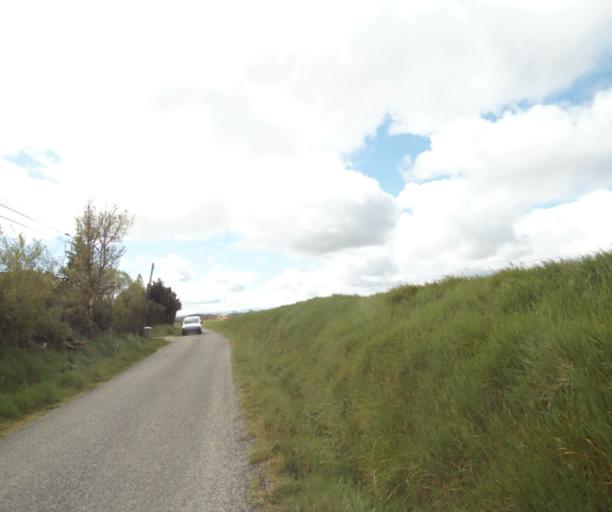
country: FR
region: Midi-Pyrenees
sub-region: Departement de l'Ariege
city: Saverdun
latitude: 43.2248
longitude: 1.5782
